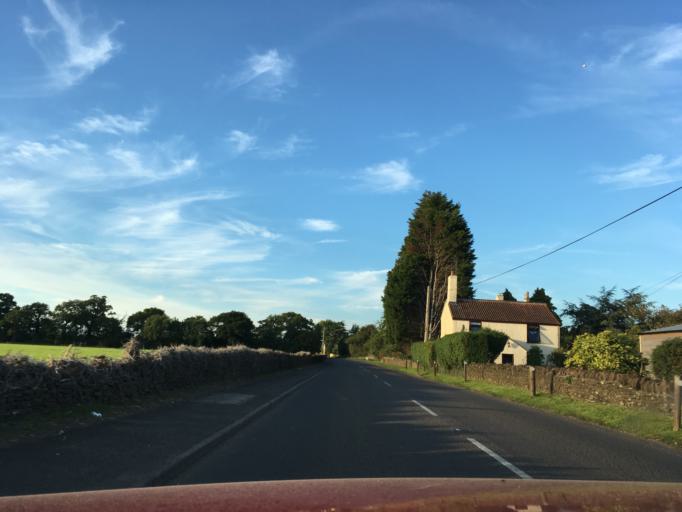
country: GB
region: England
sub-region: South Gloucestershire
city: Yate
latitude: 51.5608
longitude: -2.4514
